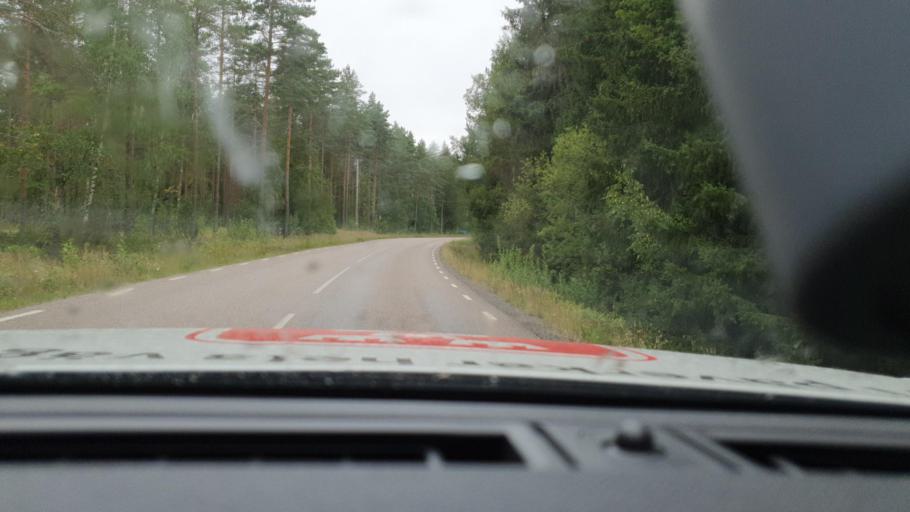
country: SE
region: Uppsala
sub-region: Heby Kommun
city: OEstervala
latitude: 60.0948
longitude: 17.1624
